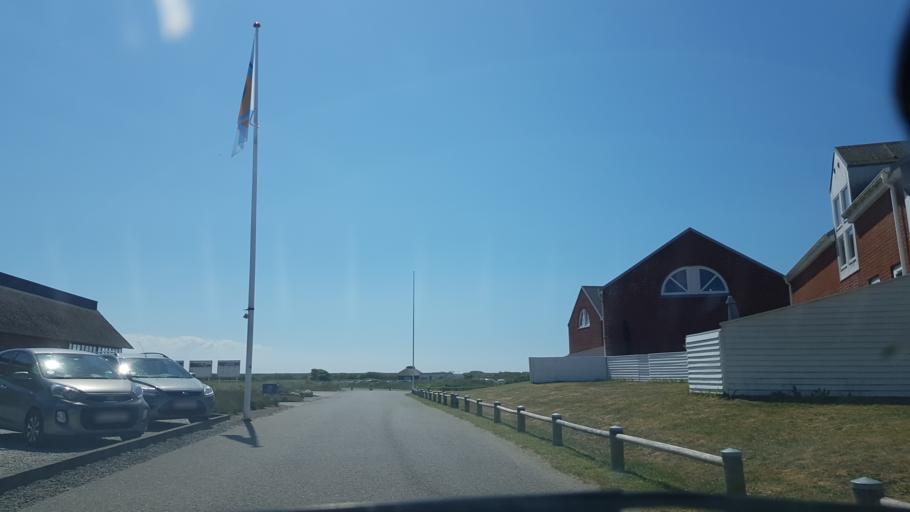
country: DE
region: Schleswig-Holstein
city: List
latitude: 55.0856
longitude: 8.5512
